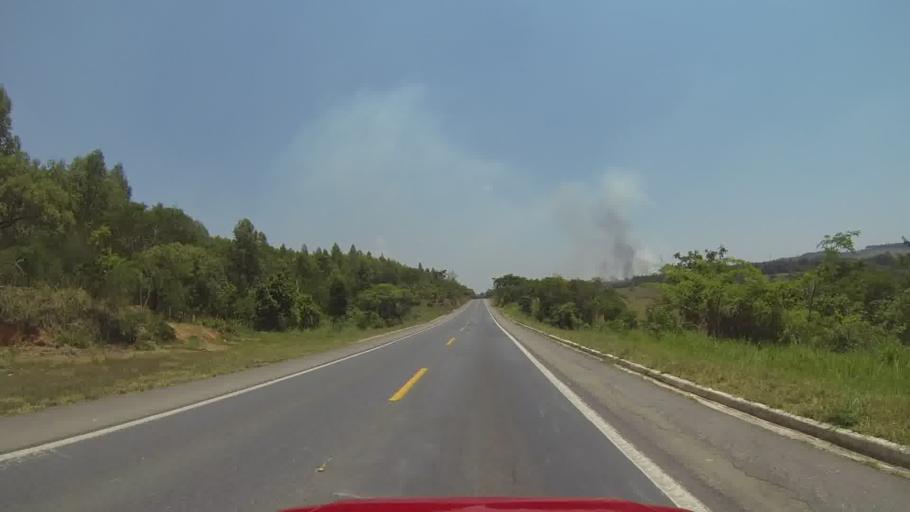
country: BR
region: Minas Gerais
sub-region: Itapecerica
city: Itapecerica
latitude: -20.3429
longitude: -45.2578
